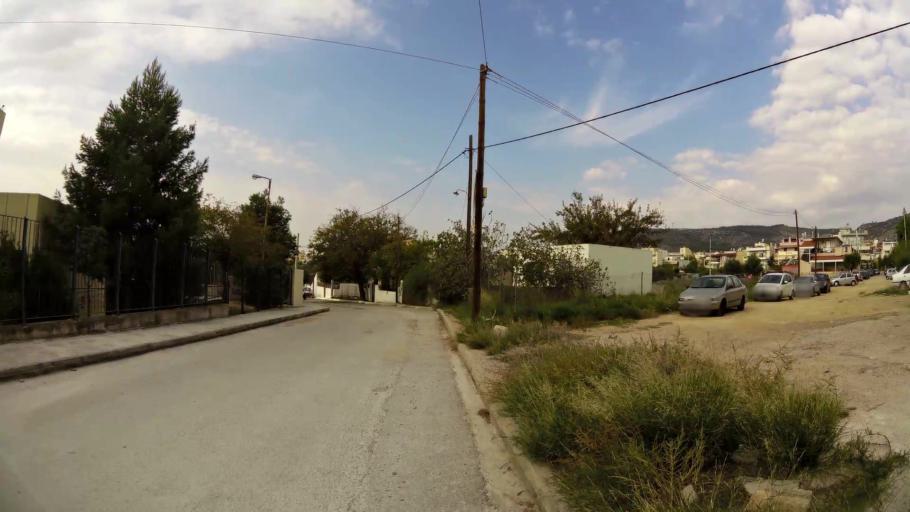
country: GR
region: Attica
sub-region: Nomarchia Athinas
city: Kamateron
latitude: 38.0512
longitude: 23.7044
